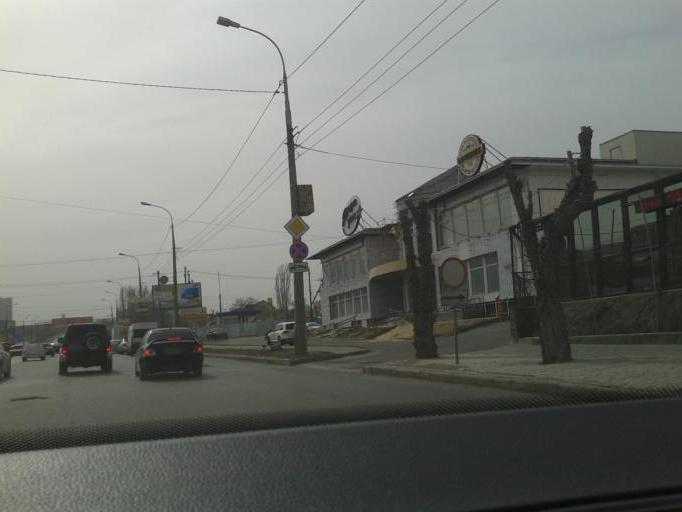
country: RU
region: Volgograd
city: Volgograd
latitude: 48.7051
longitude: 44.4834
